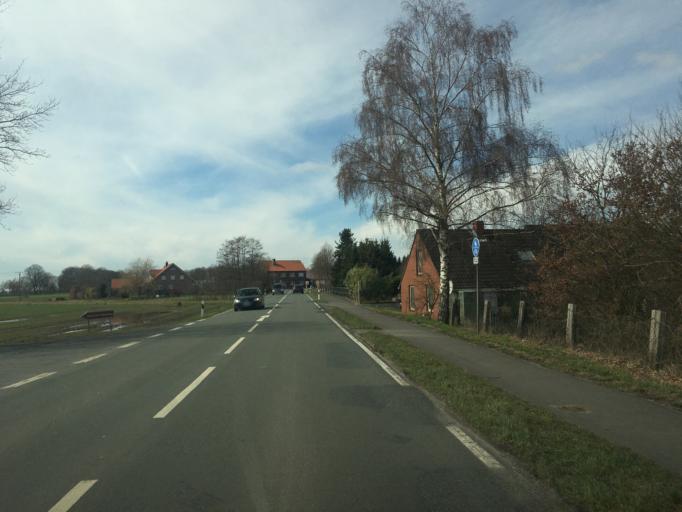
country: DE
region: North Rhine-Westphalia
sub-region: Regierungsbezirk Munster
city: Ascheberg
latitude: 51.7275
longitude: 7.6204
